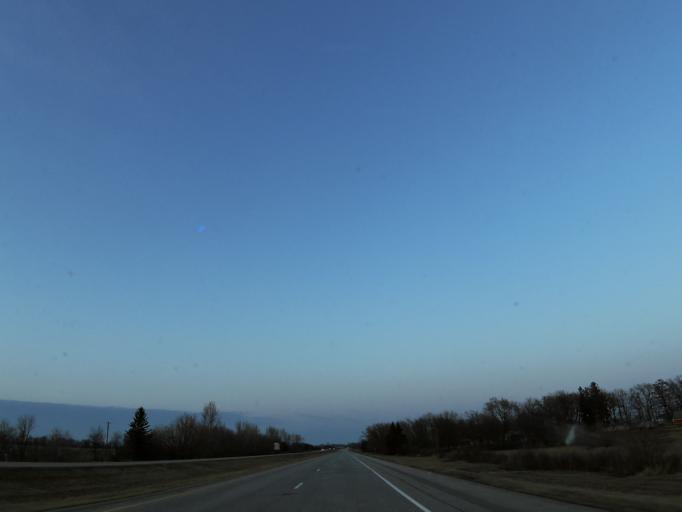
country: US
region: Minnesota
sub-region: Mower County
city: Grand Meadow
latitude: 43.6869
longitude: -92.7336
